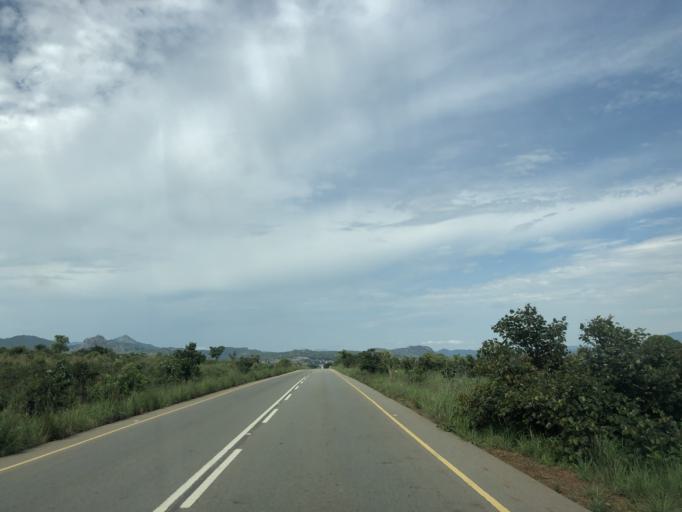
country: AO
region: Cuanza Sul
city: Quibala
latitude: -10.7332
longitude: 15.0179
